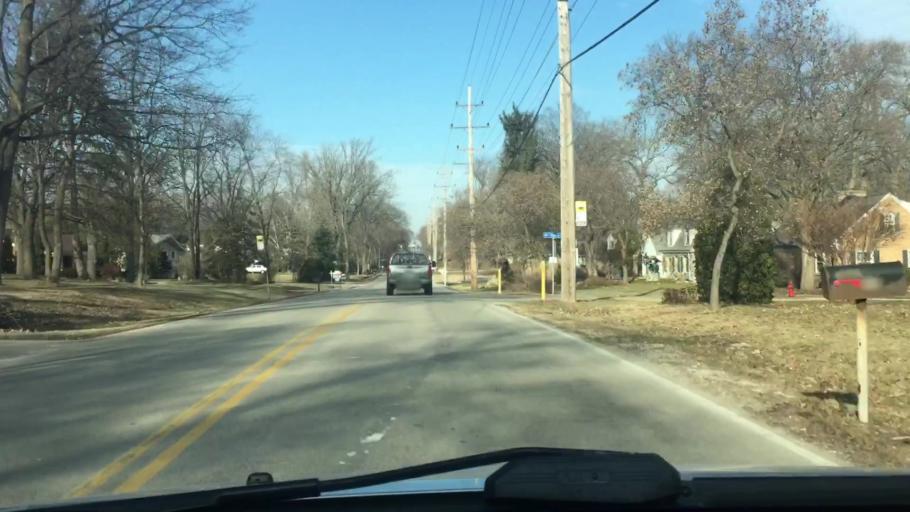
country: US
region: Wisconsin
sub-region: Waukesha County
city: Elm Grove
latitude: 43.0488
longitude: -88.0669
